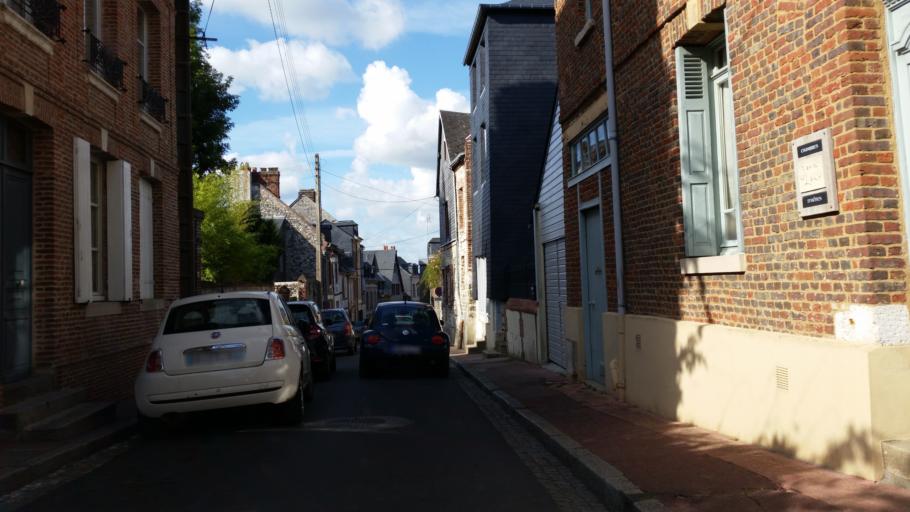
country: FR
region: Lower Normandy
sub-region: Departement du Calvados
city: Honfleur
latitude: 49.4163
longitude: 0.2331
